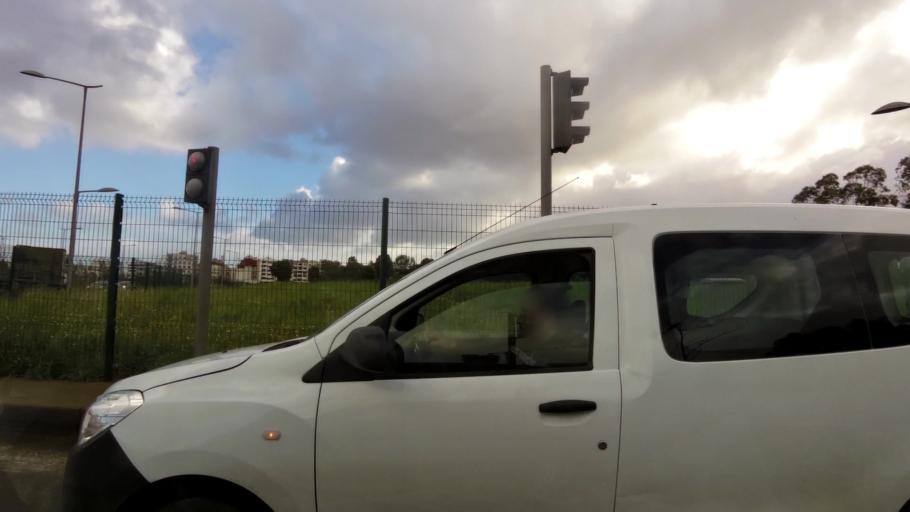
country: MA
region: Grand Casablanca
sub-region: Casablanca
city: Casablanca
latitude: 33.5628
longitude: -7.6545
